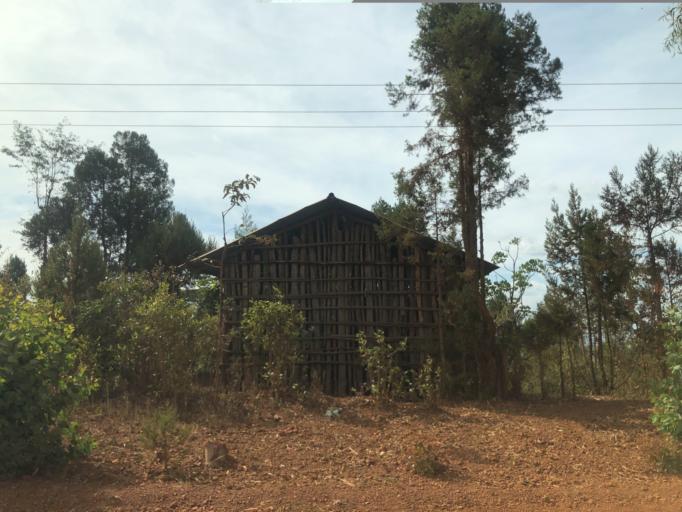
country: ET
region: Southern Nations, Nationalities, and People's Region
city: Konso
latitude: 5.3168
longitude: 37.3881
